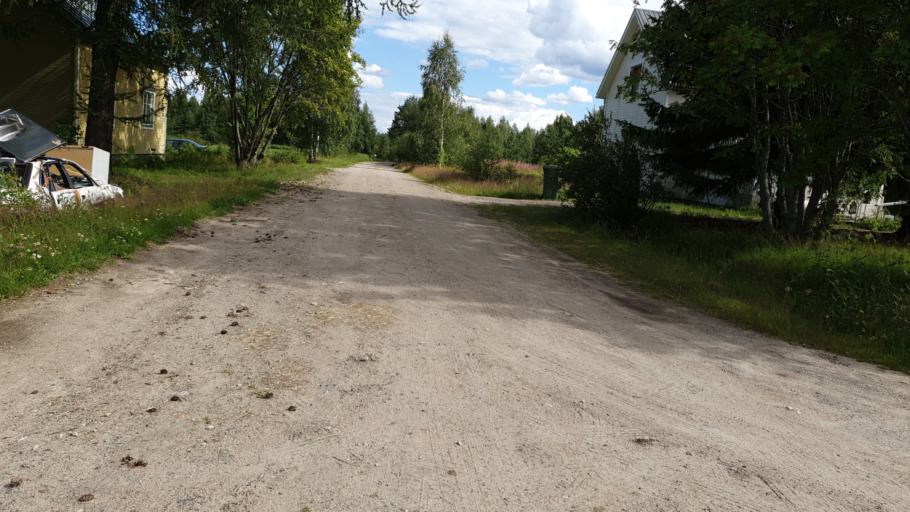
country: FI
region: Kainuu
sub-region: Kehys-Kainuu
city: Kuhmo
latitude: 64.1133
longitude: 29.5234
